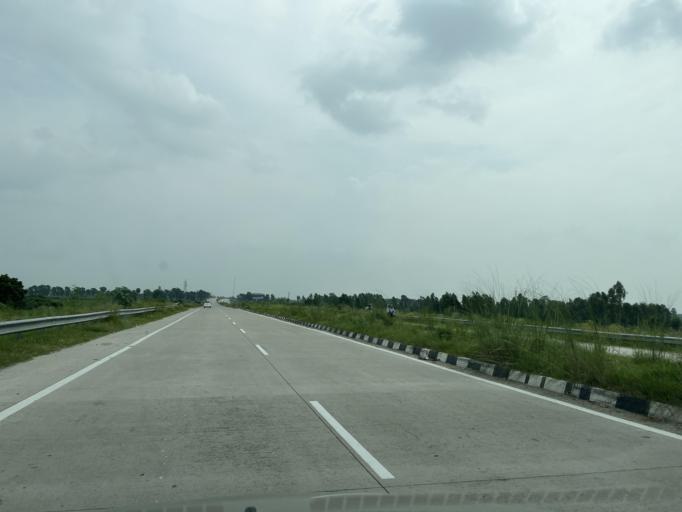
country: IN
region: Uttarakhand
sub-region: Udham Singh Nagar
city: Kashipur
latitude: 29.1974
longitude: 78.9351
